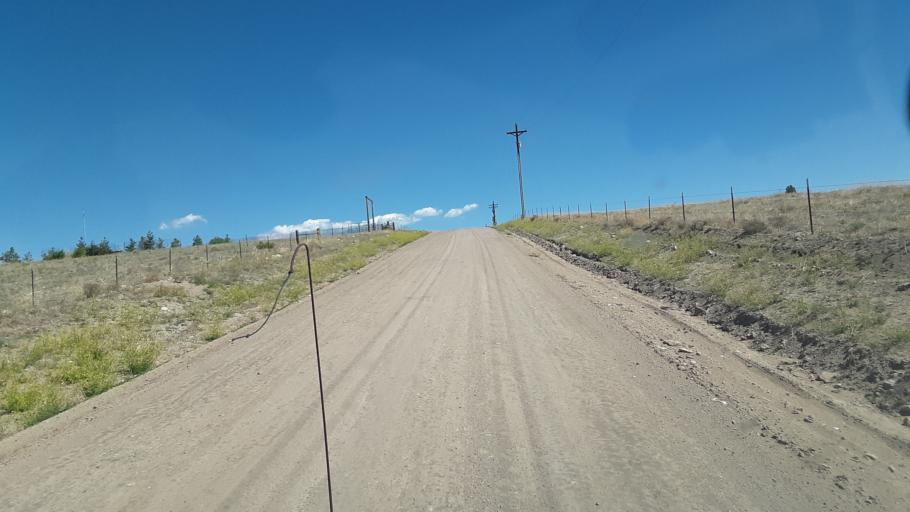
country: US
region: Colorado
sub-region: Custer County
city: Westcliffe
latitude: 38.2804
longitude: -105.5009
